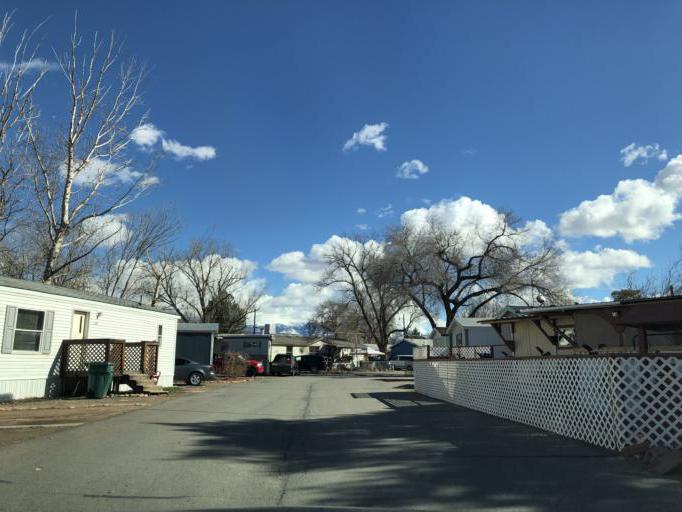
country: US
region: Utah
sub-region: Grand County
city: Moab
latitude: 38.5779
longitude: -109.5626
